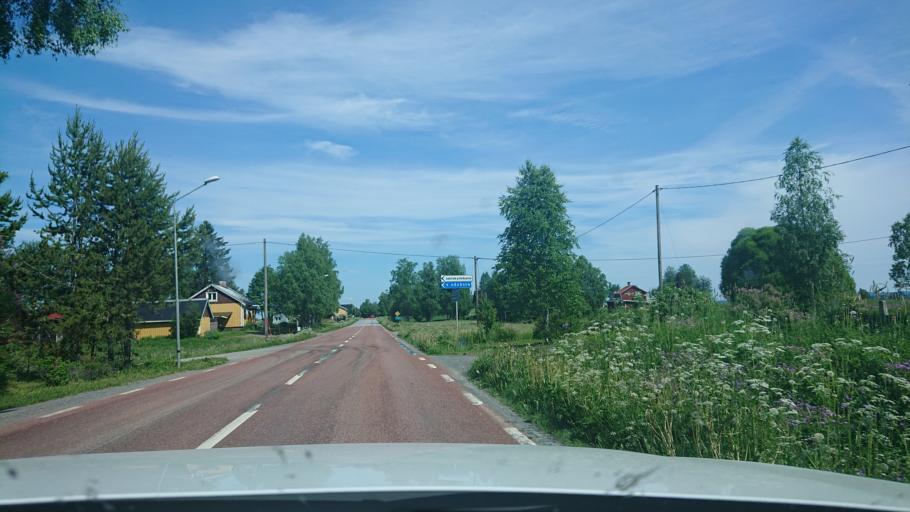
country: SE
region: Jaemtland
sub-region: Stroemsunds Kommun
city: Stroemsund
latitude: 63.7282
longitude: 15.4837
